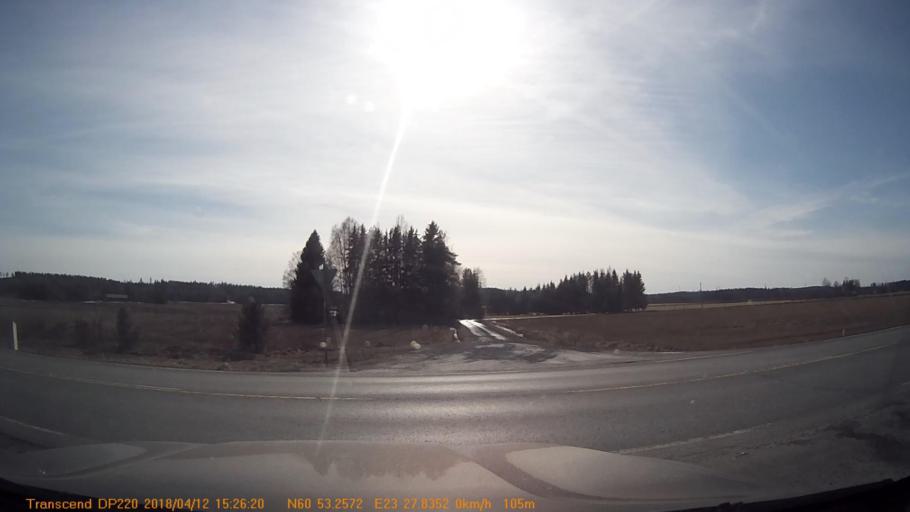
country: FI
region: Haeme
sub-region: Forssa
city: Jokioinen
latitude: 60.8879
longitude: 23.4645
